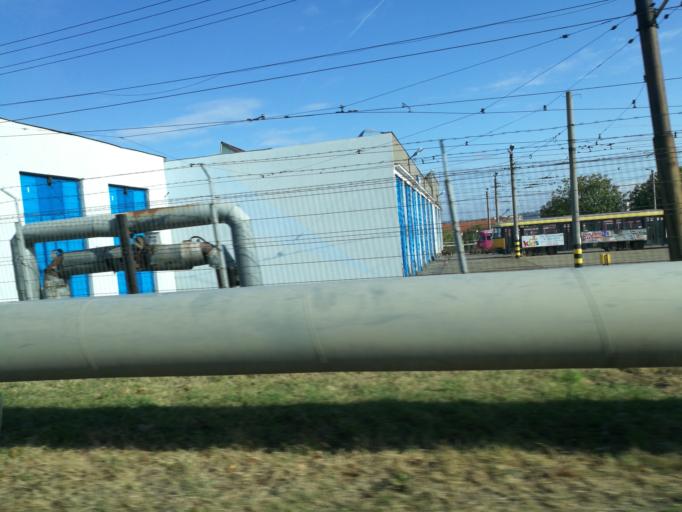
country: RO
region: Bihor
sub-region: Comuna Biharea
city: Oradea
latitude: 47.0388
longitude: 21.9361
